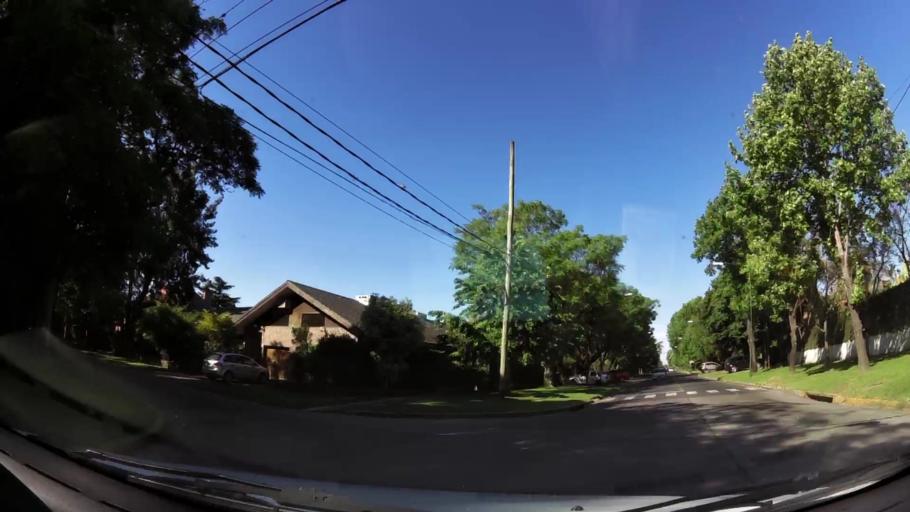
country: AR
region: Buenos Aires
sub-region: Partido de San Isidro
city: San Isidro
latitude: -34.4835
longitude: -58.5415
